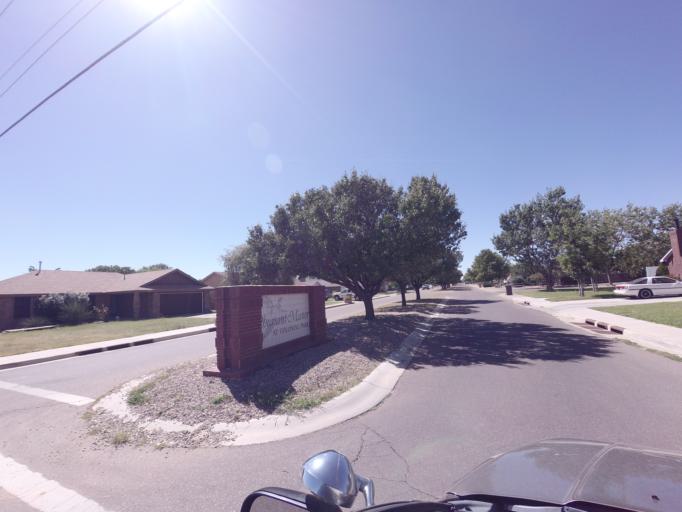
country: US
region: New Mexico
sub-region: Curry County
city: Clovis
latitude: 34.4457
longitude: -103.1786
